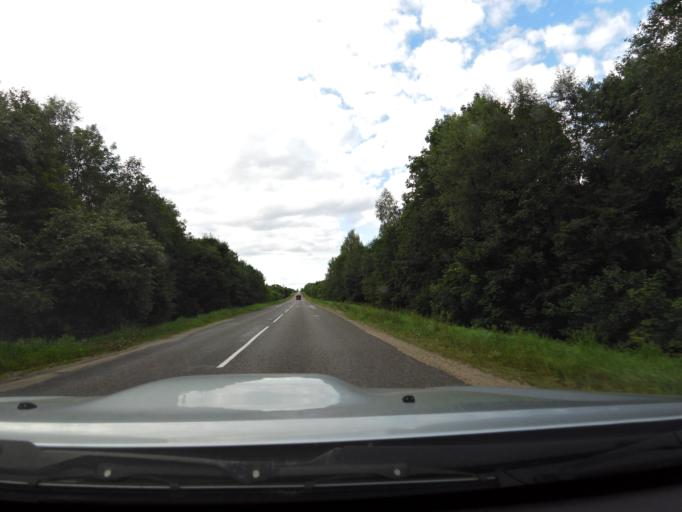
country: LV
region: Akniste
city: Akniste
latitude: 56.0161
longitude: 25.9255
